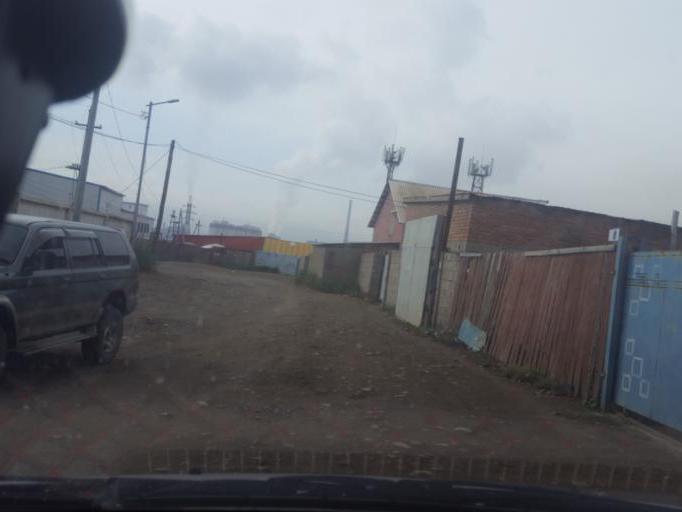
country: MN
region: Ulaanbaatar
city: Ulaanbaatar
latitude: 47.9194
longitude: 106.7990
